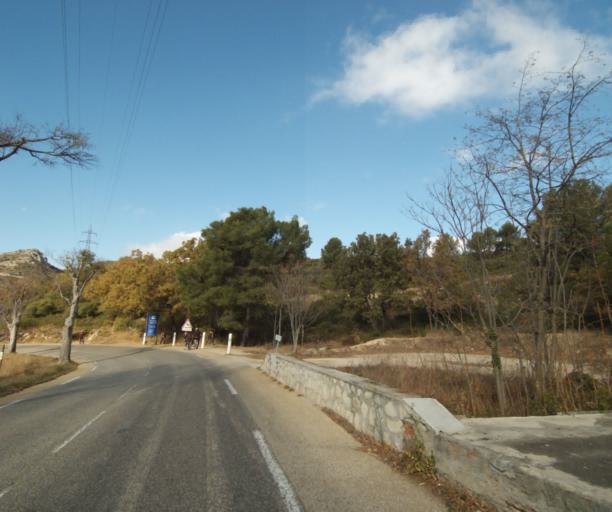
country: FR
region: Provence-Alpes-Cote d'Azur
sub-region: Departement des Bouches-du-Rhone
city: Cadolive
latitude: 43.3847
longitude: 5.5531
